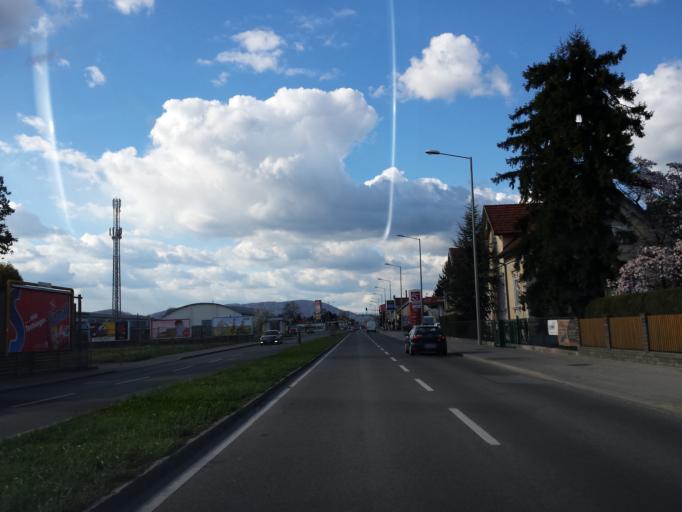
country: AT
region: Styria
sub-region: Politischer Bezirk Graz-Umgebung
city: Feldkirchen bei Graz
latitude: 47.0190
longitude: 15.4389
